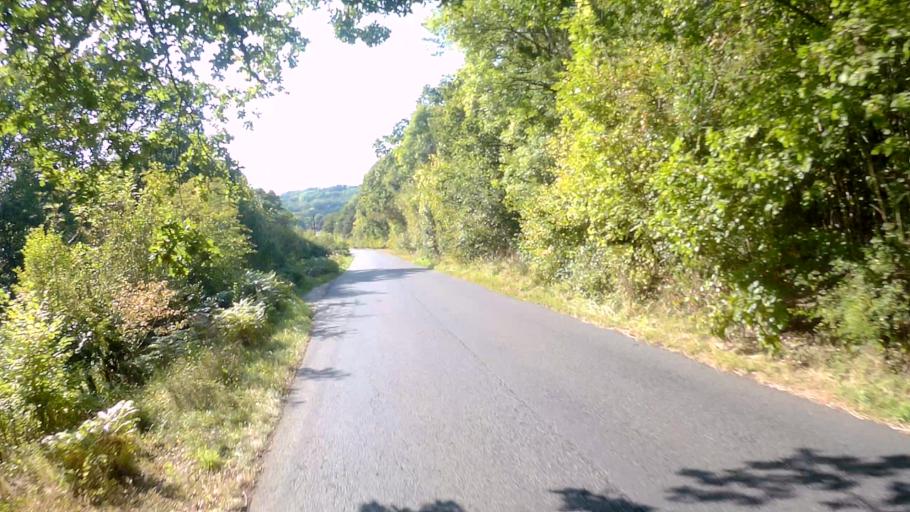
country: GB
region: England
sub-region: Hampshire
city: Kingsley
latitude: 51.1685
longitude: -0.8521
